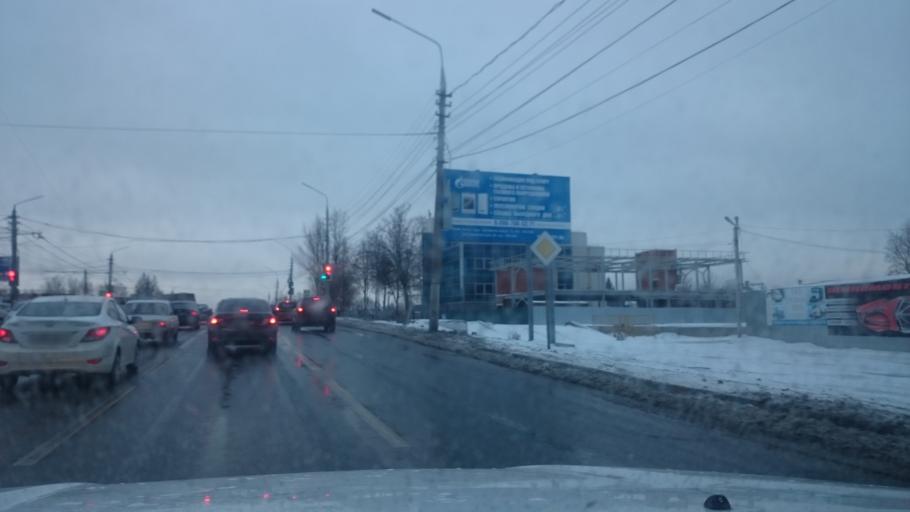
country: RU
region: Tula
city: Mendeleyevskiy
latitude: 54.1446
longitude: 37.5819
